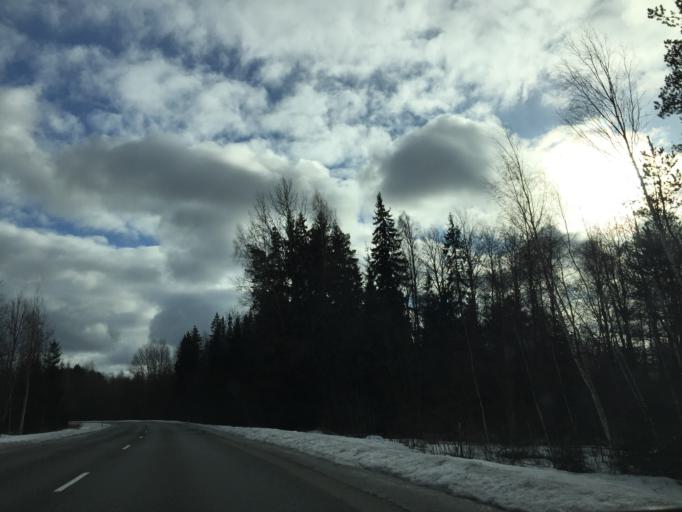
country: LV
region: Aloja
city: Staicele
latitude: 57.8506
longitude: 24.7111
